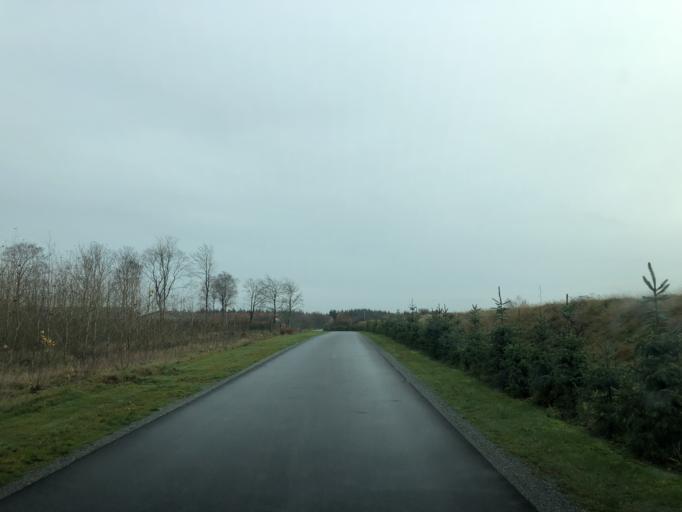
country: DK
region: Central Jutland
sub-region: Ikast-Brande Kommune
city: Bording Kirkeby
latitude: 56.0629
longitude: 9.3705
